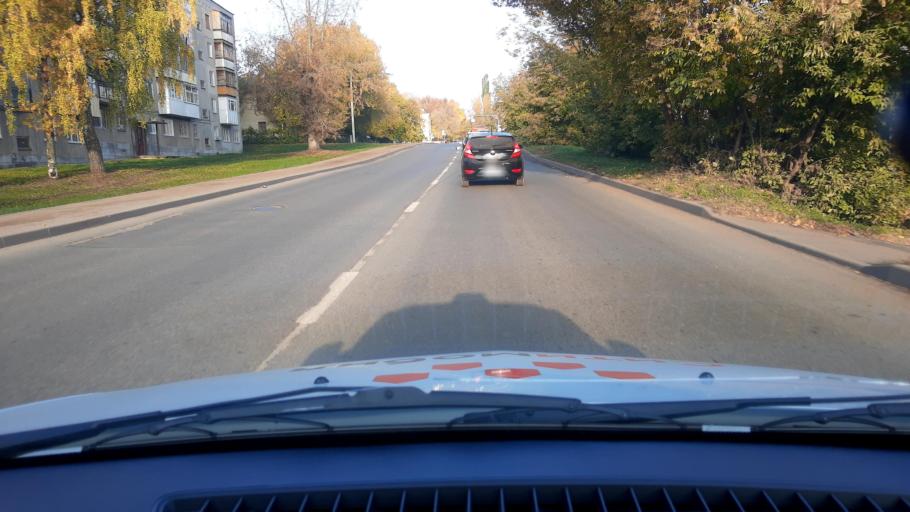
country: RU
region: Bashkortostan
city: Ufa
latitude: 54.8218
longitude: 56.1146
